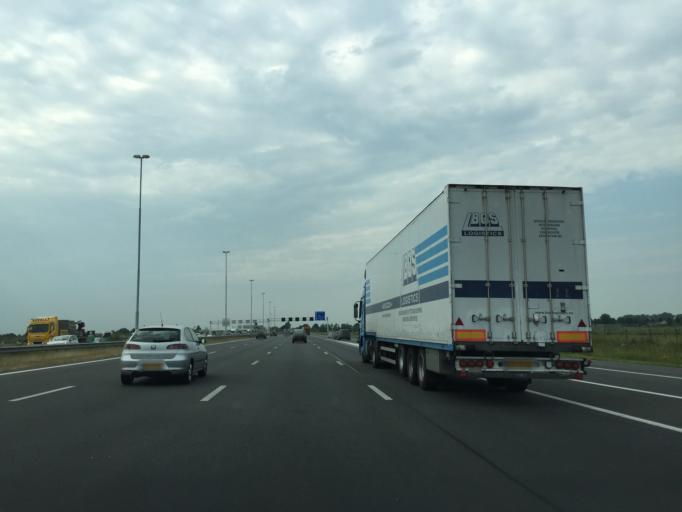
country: NL
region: Gelderland
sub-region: Gemeente Culemborg
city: Culemborg
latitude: 51.9310
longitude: 5.1627
